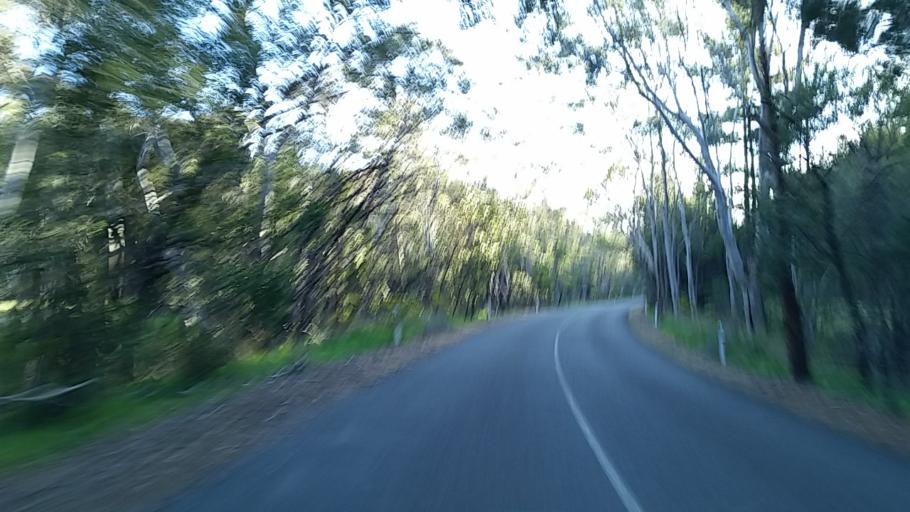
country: AU
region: South Australia
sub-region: Mount Barker
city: Meadows
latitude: -35.2315
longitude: 138.7221
